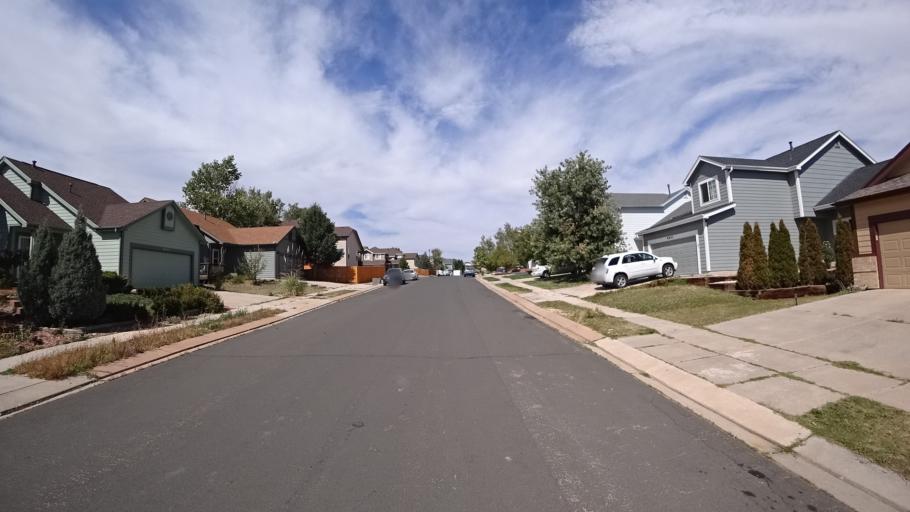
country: US
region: Colorado
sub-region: El Paso County
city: Cimarron Hills
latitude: 38.8990
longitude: -104.7157
